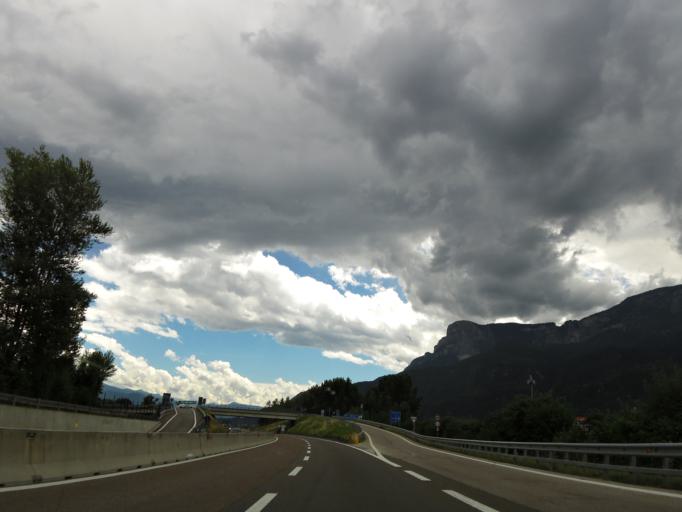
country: IT
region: Trentino-Alto Adige
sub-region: Bolzano
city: Nalles
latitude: 46.5570
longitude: 11.2164
